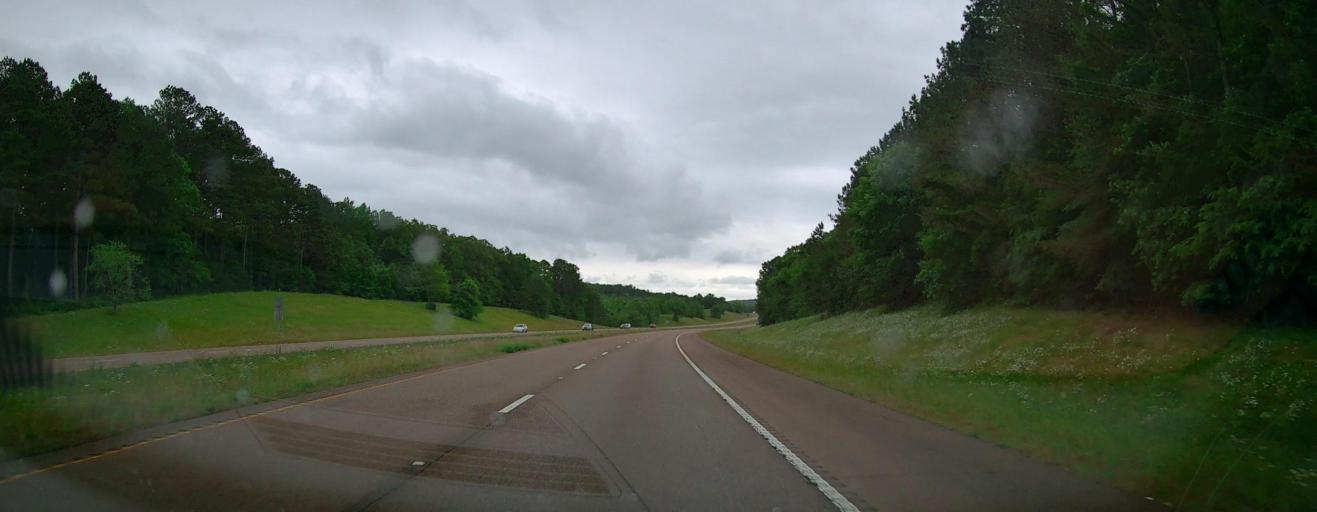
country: US
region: Mississippi
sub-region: Benton County
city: Ashland
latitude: 34.6283
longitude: -89.2099
